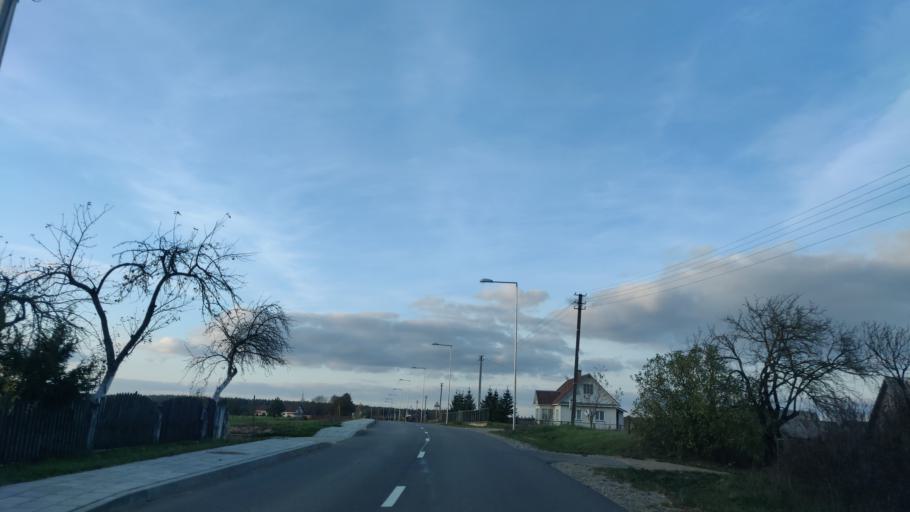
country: LT
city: Lentvaris
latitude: 54.5884
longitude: 25.0507
